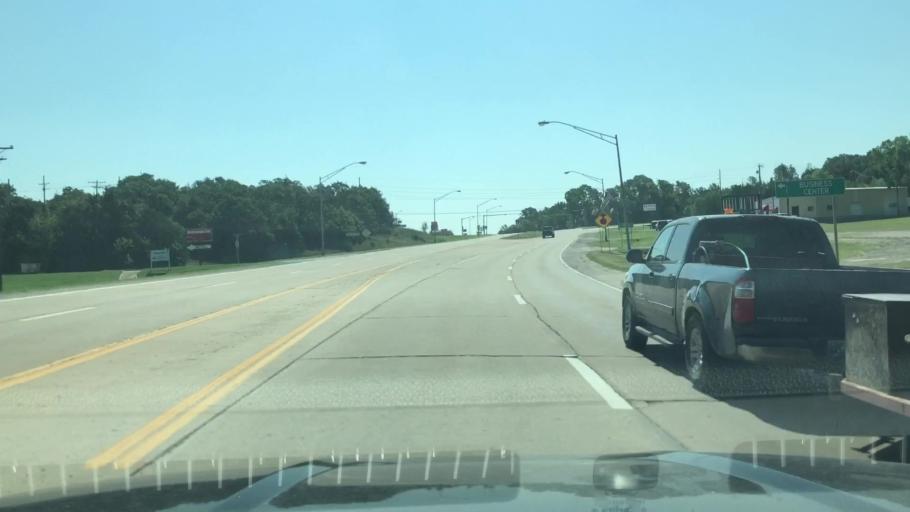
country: US
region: Oklahoma
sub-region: Creek County
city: Drumright
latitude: 35.9883
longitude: -96.5868
